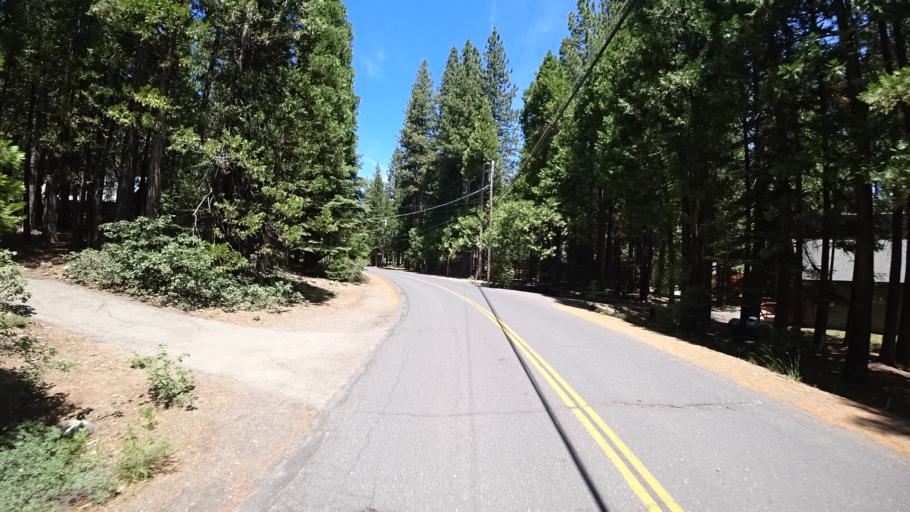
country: US
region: California
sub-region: Calaveras County
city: Arnold
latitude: 38.3081
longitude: -120.2608
